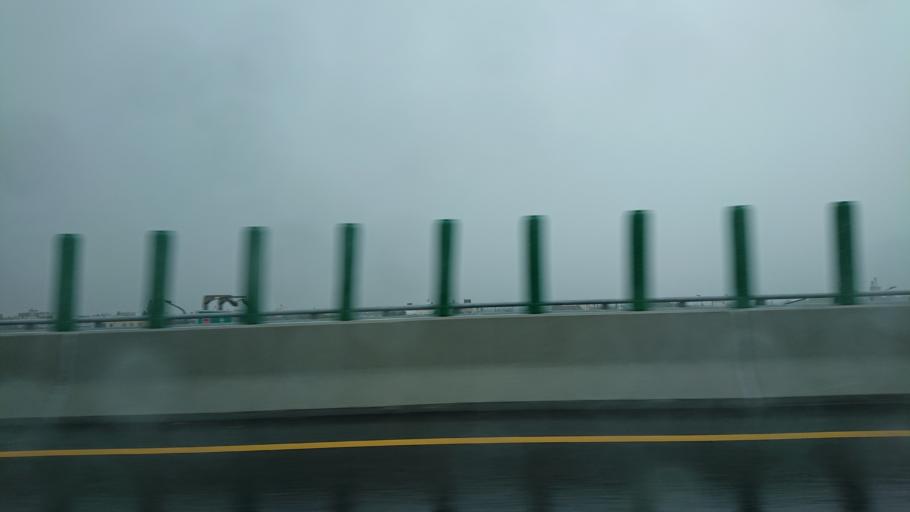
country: TW
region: Taiwan
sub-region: Changhua
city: Chang-hua
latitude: 23.9393
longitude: 120.3223
